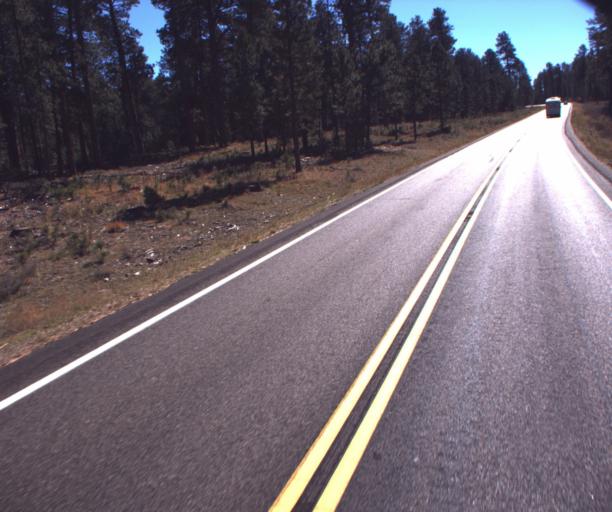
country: US
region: Arizona
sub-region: Coconino County
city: Fredonia
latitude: 36.6506
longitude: -112.1834
